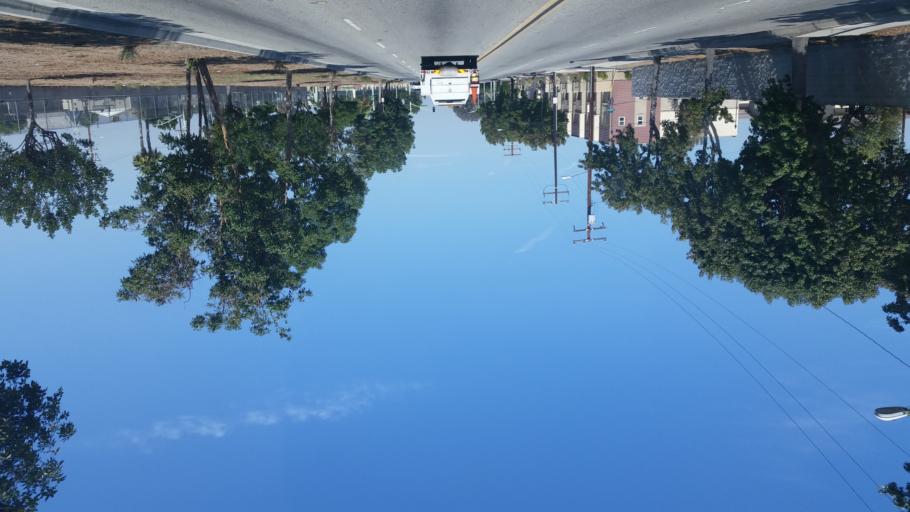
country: US
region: California
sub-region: Los Angeles County
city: Compton
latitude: 33.8907
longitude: -118.2197
